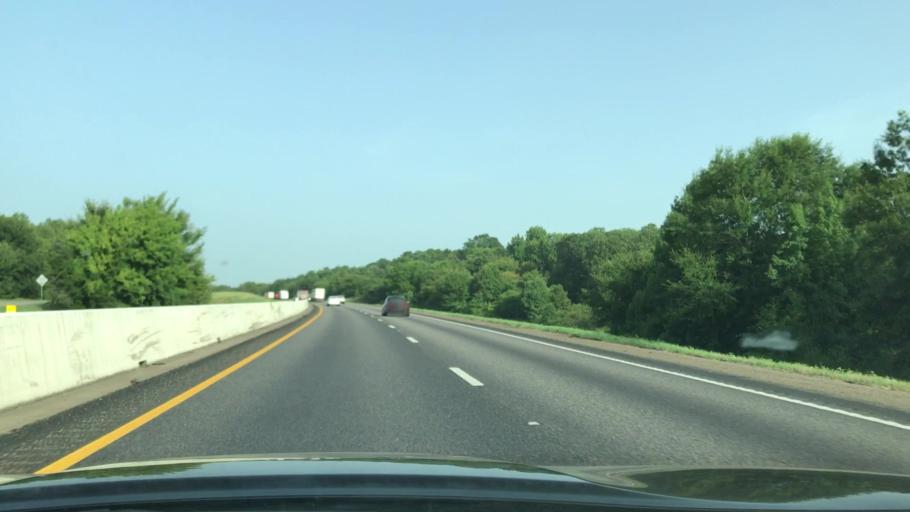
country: US
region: Texas
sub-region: Smith County
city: Lindale
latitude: 32.4679
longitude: -95.3423
